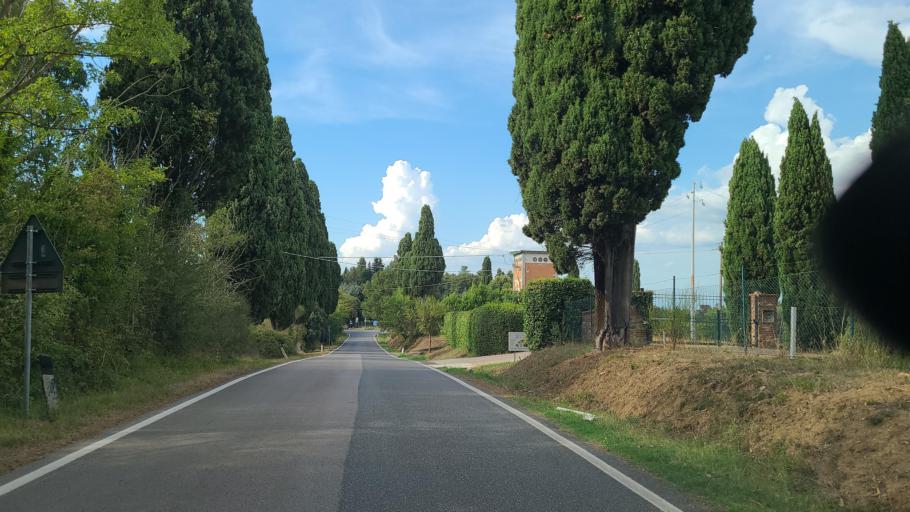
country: IT
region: Tuscany
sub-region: Province of Florence
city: Gambassi Terme
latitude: 43.4793
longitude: 10.9543
